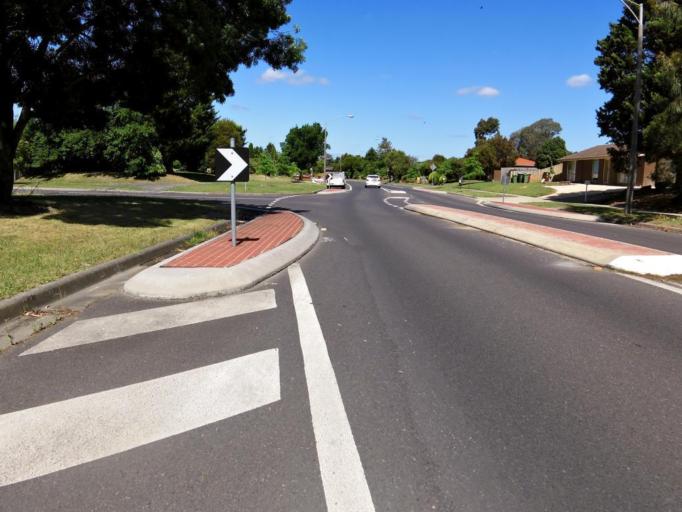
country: AU
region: Victoria
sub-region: Casey
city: Endeavour Hills
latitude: -37.9682
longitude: 145.2562
